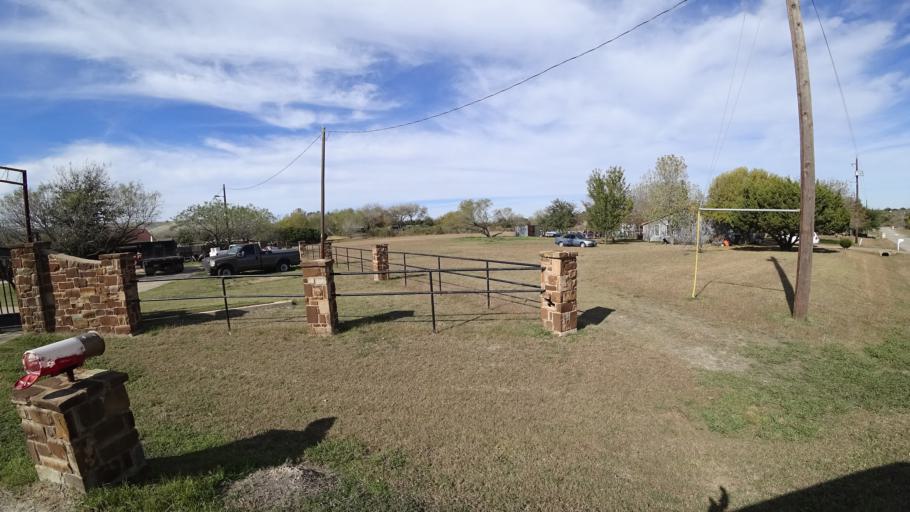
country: US
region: Texas
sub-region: Travis County
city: Onion Creek
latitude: 30.1078
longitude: -97.7489
